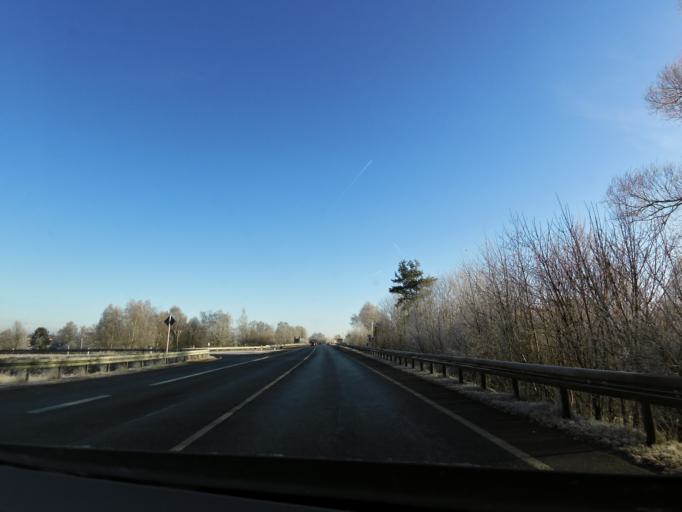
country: DE
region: Bavaria
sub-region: Upper Franconia
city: Marktredwitz
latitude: 50.0147
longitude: 12.0994
